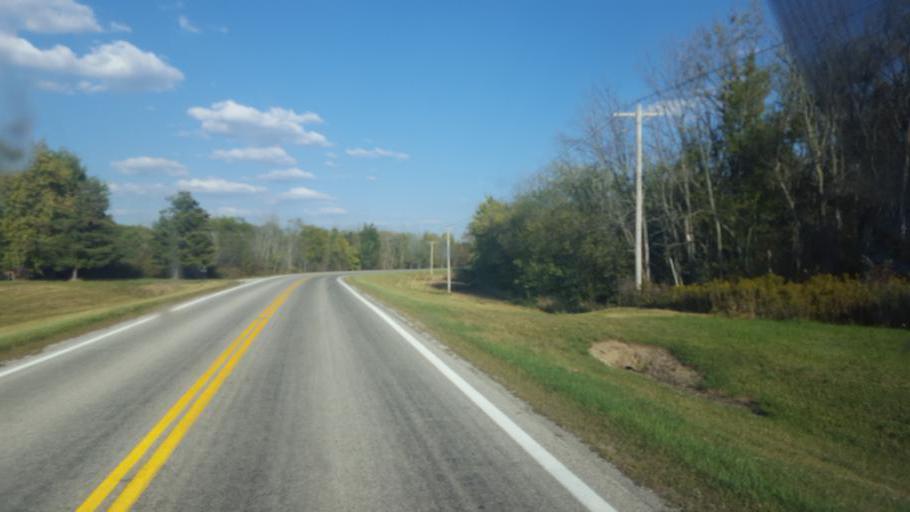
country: US
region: Ohio
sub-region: Union County
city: Richwood
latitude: 40.5789
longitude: -83.3601
